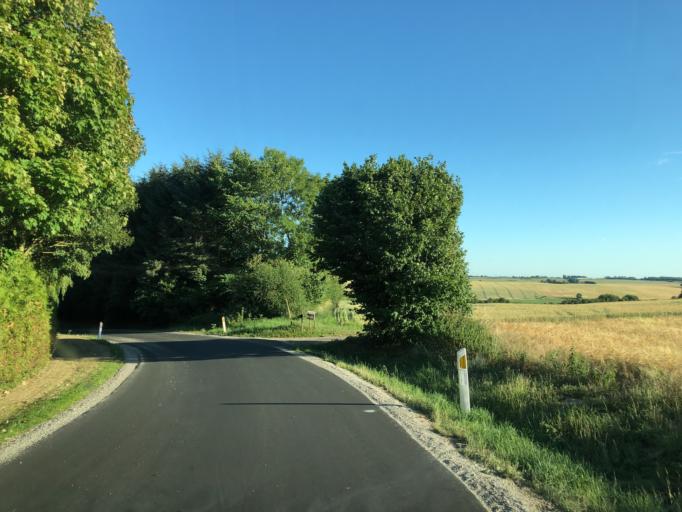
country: DK
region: Central Jutland
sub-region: Horsens Kommune
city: Horsens
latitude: 55.9546
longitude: 9.8420
